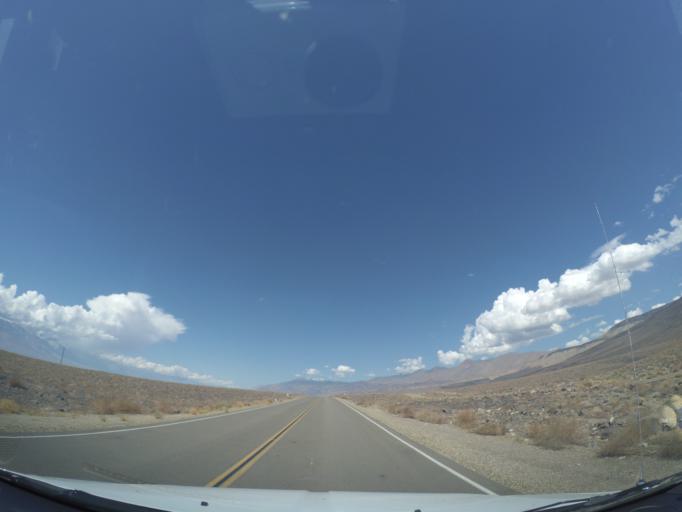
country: US
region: California
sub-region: Inyo County
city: Lone Pine
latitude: 36.4114
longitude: -117.8118
